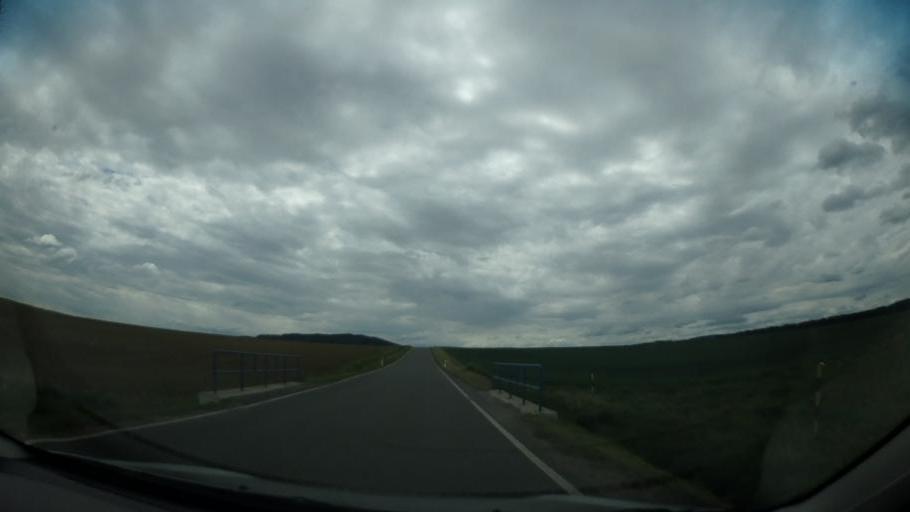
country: CZ
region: Pardubicky
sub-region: Okres Svitavy
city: Moravska Trebova
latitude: 49.8109
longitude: 16.6898
